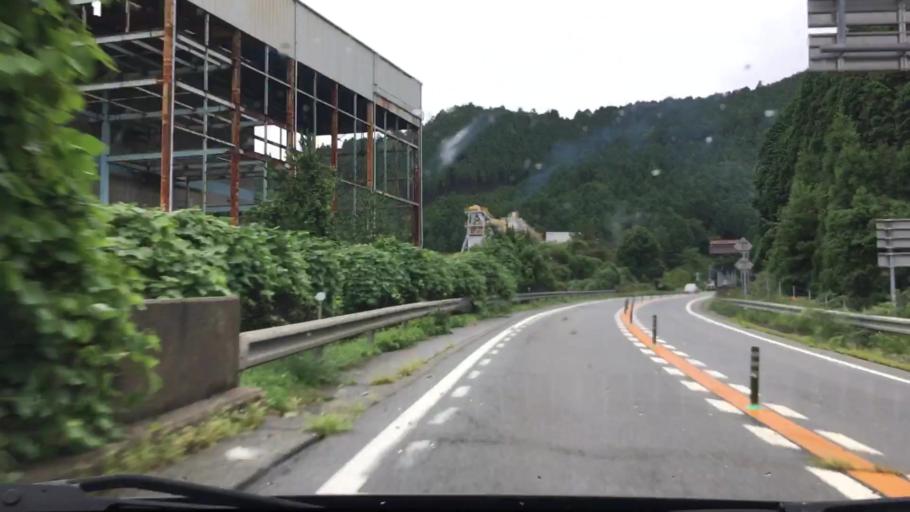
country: JP
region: Hyogo
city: Nishiwaki
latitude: 35.1483
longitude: 134.7880
